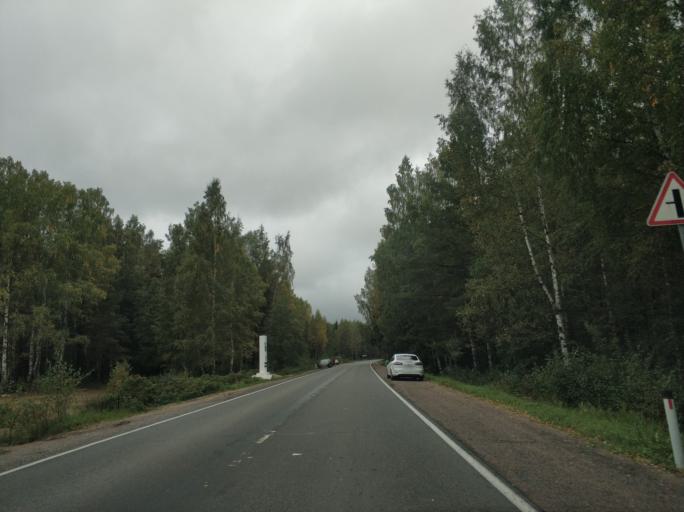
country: RU
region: Leningrad
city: Borisova Griva
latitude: 60.0889
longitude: 30.8657
